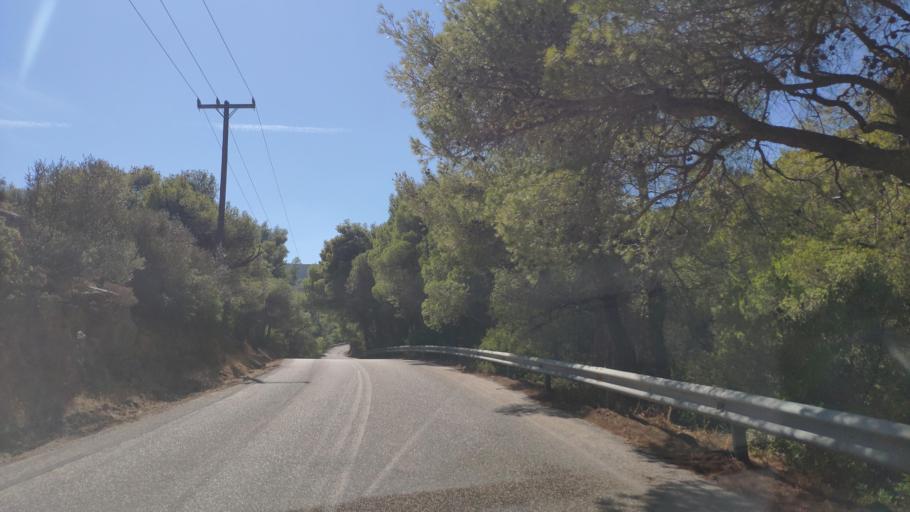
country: GR
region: Attica
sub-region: Nomarchia Anatolikis Attikis
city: Limin Mesoyaias
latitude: 37.8433
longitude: 24.0147
